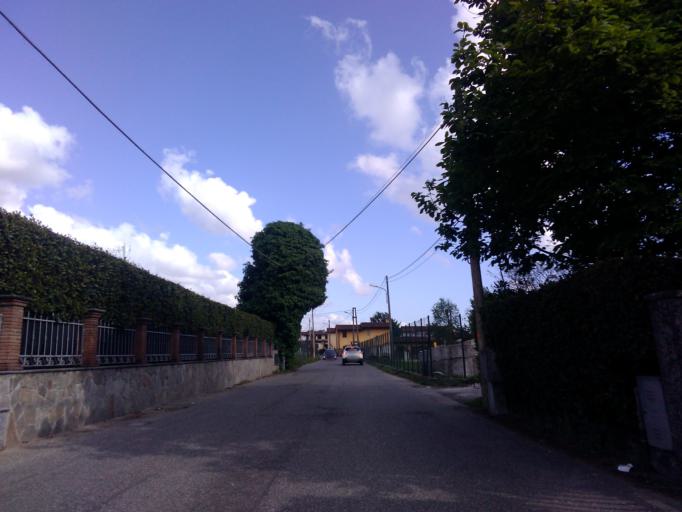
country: IT
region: Tuscany
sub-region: Provincia di Massa-Carrara
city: Capanne-Prato-Cinquale
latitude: 44.0061
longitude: 10.1491
